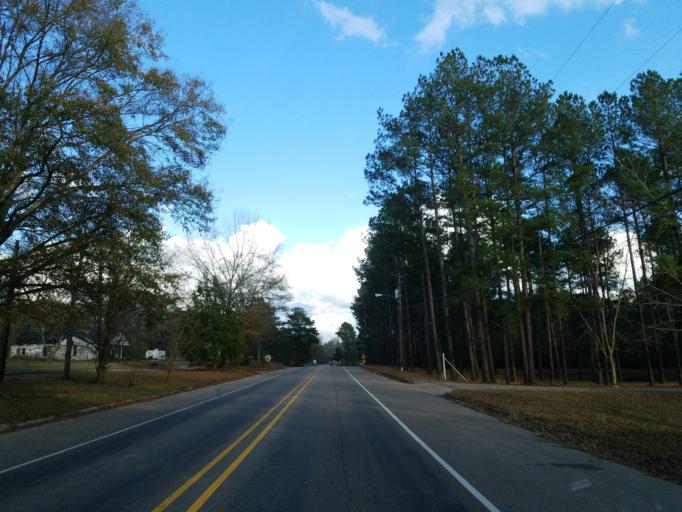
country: US
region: Mississippi
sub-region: Jones County
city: Sharon
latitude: 31.7879
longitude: -89.0410
